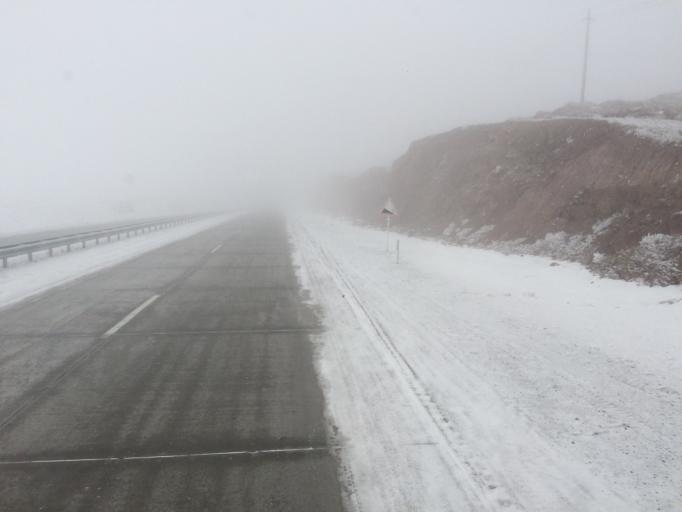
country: KZ
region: Zhambyl
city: Georgiyevka
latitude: 43.4304
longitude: 74.9492
